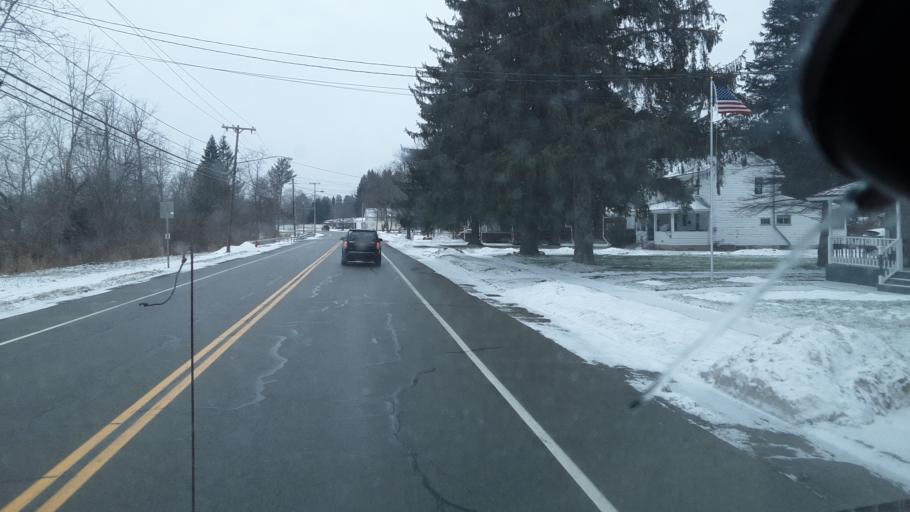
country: US
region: New York
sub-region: Allegany County
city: Belmont
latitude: 42.2235
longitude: -78.0252
